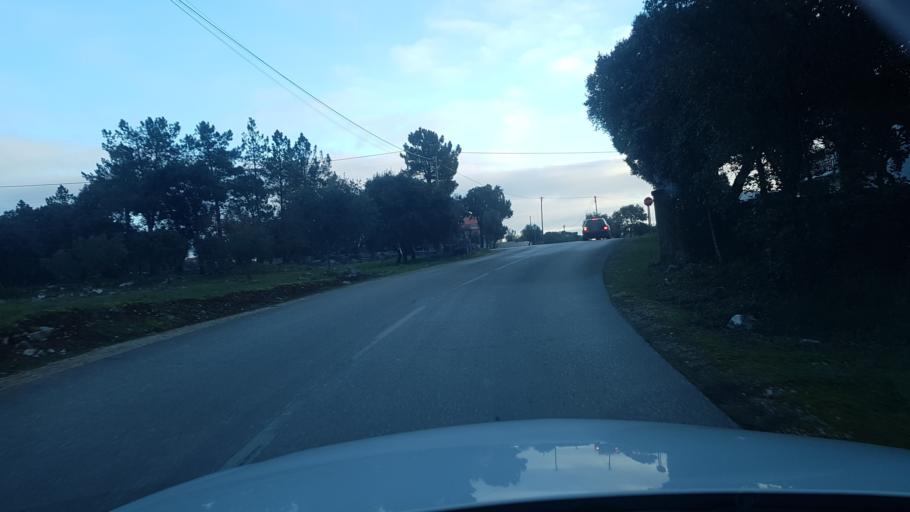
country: PT
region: Santarem
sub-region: Ourem
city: Fatima
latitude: 39.6000
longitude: -8.6498
